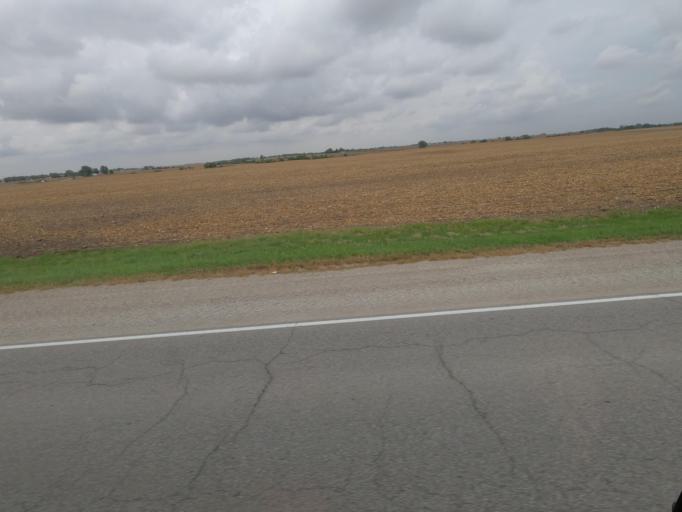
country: US
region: Iowa
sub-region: Wapello County
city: Ottumwa
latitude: 40.9504
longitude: -92.2341
